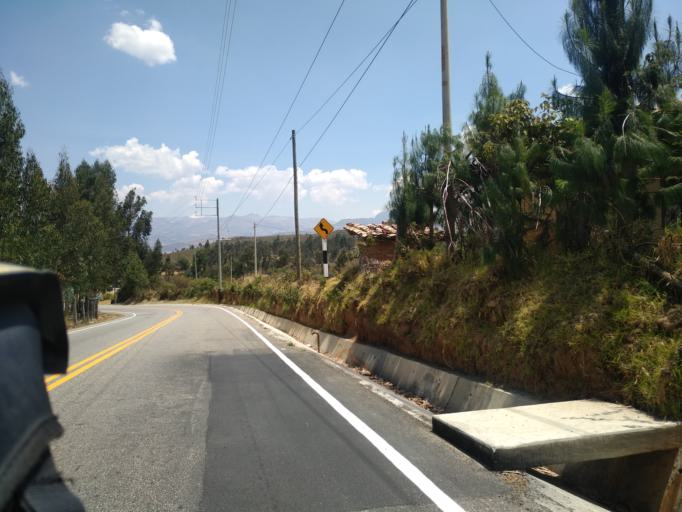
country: PE
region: Cajamarca
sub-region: San Marcos
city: San Marcos
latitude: -7.2923
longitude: -78.2056
